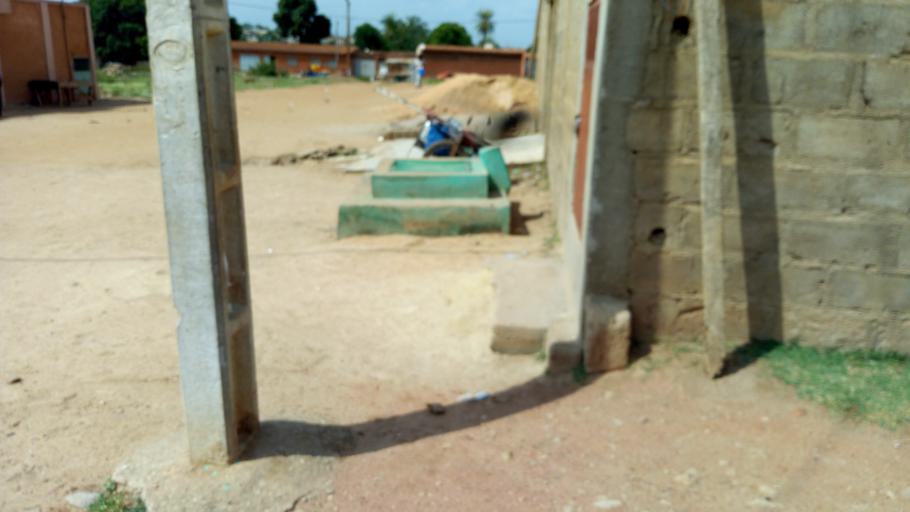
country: CI
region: Vallee du Bandama
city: Bouake
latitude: 7.7219
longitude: -5.0392
